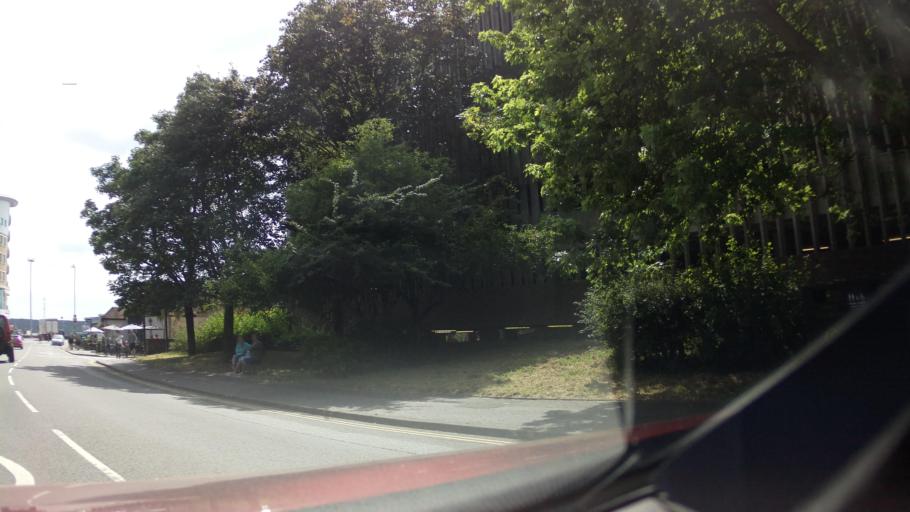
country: GB
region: England
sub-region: Poole
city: Poole
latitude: 50.7134
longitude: -1.9855
